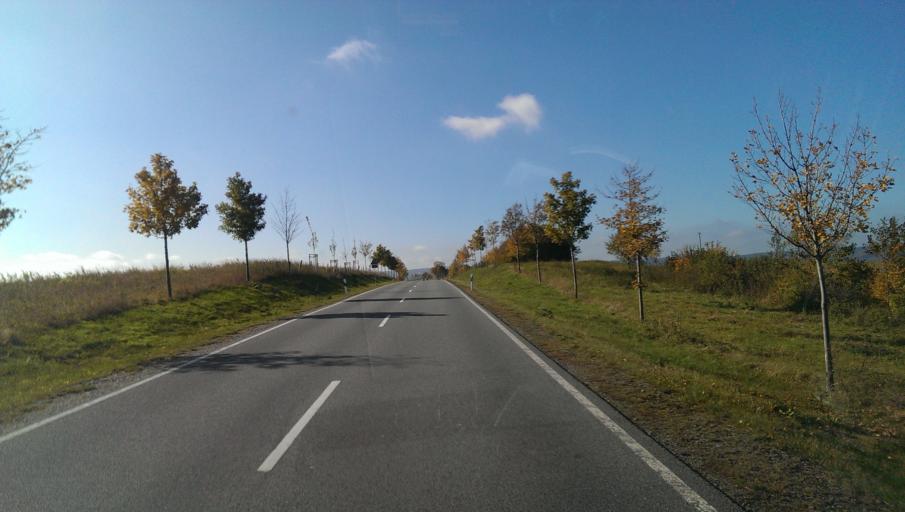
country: DE
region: Saxony
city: Liebstadt
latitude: 50.7927
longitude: 13.8754
